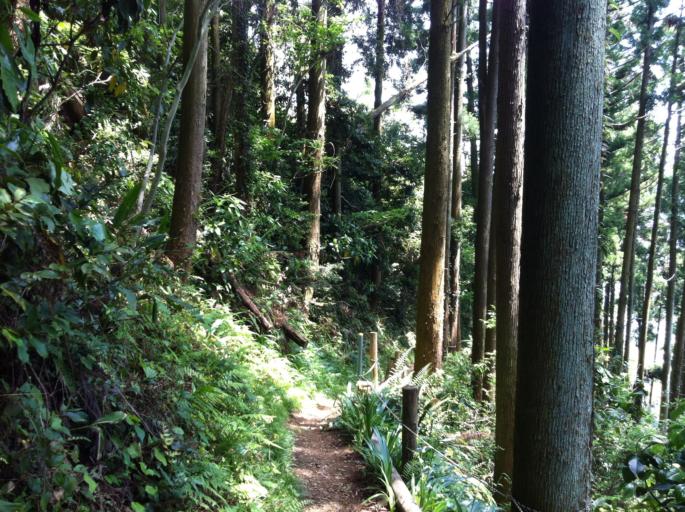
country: JP
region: Shizuoka
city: Shizuoka-shi
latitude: 35.0302
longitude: 138.4344
